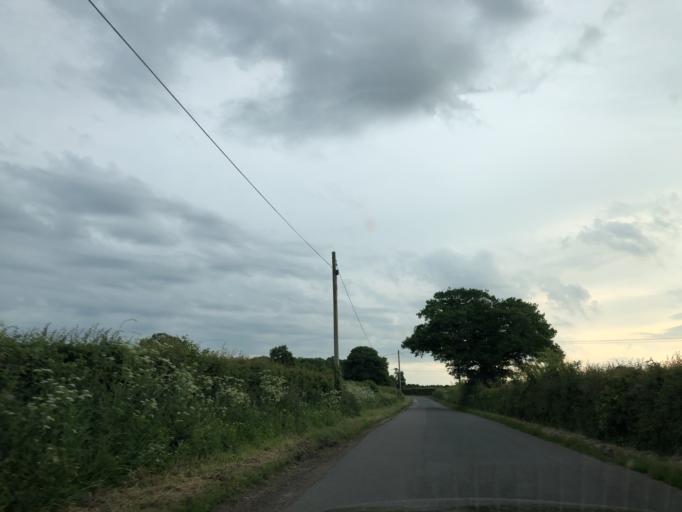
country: GB
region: England
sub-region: Warwickshire
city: Warwick
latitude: 52.2897
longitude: -1.6304
